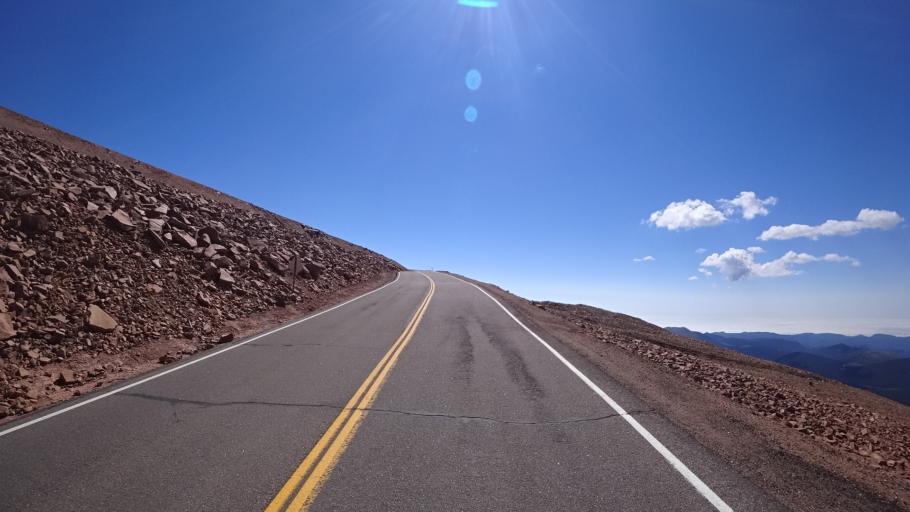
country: US
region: Colorado
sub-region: El Paso County
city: Cascade-Chipita Park
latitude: 38.8375
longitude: -105.0451
